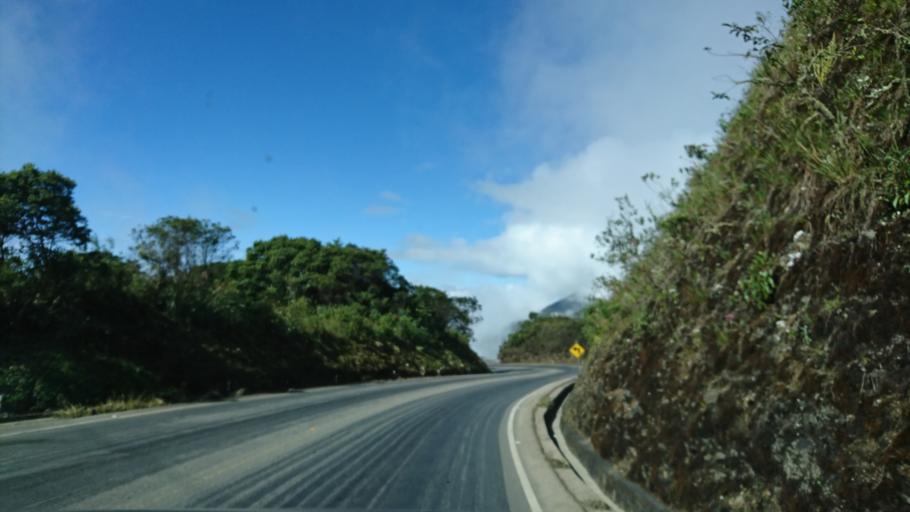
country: BO
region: La Paz
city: Coroico
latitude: -16.2248
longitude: -67.8123
